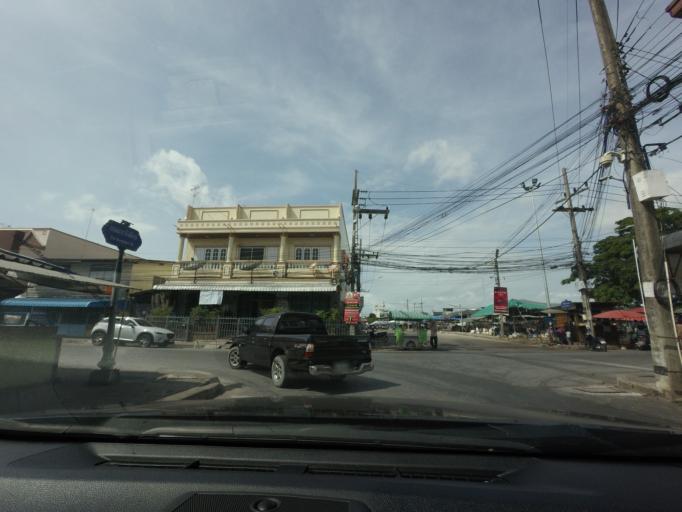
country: TH
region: Pattani
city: Pattani
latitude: 6.8629
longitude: 101.2526
